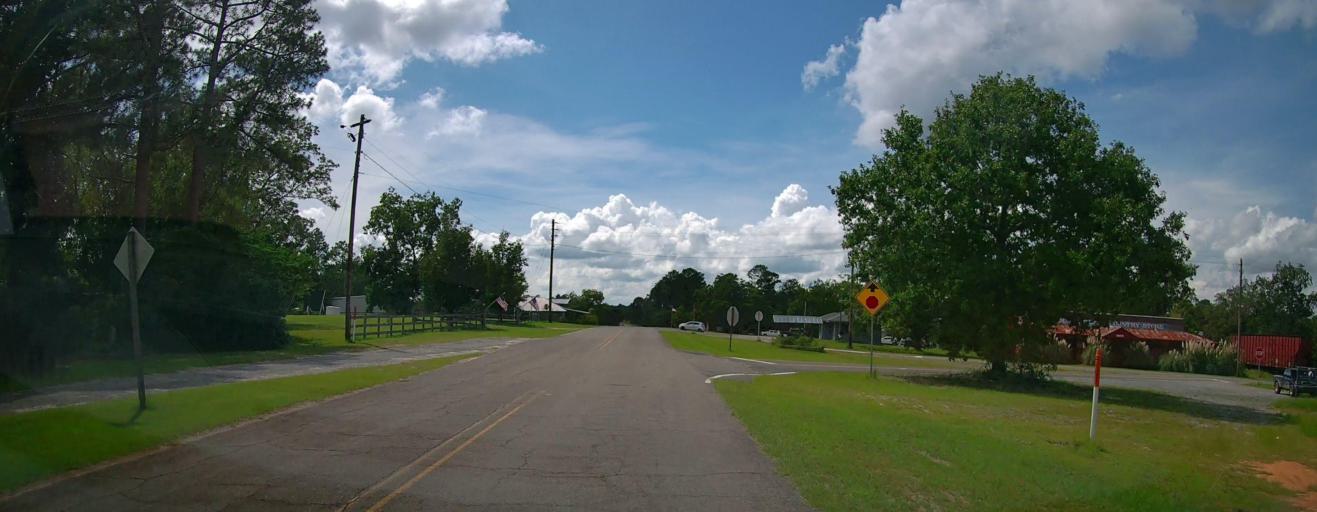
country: US
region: Georgia
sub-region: Taylor County
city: Butler
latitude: 32.5961
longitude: -84.3829
